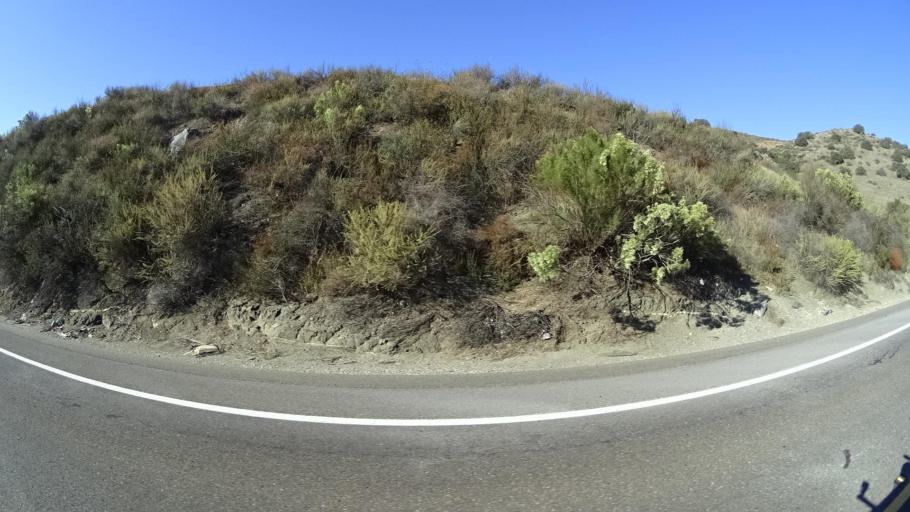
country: US
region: California
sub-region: San Diego County
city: Jamul
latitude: 32.6760
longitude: -116.8377
